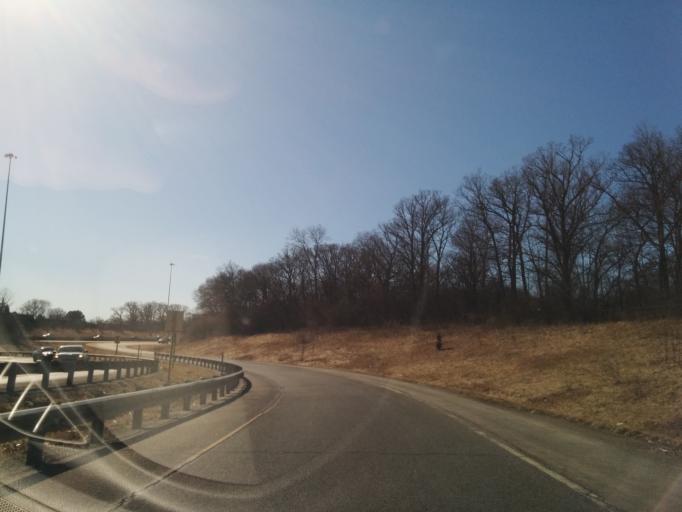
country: US
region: Illinois
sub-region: Cook County
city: Hodgkins
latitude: 41.7634
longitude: -87.8691
